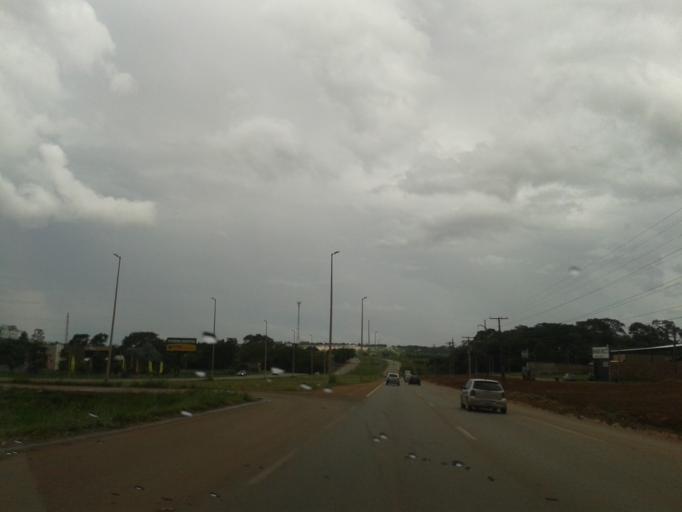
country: BR
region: Goias
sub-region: Goianira
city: Goianira
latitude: -16.5842
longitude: -49.3852
